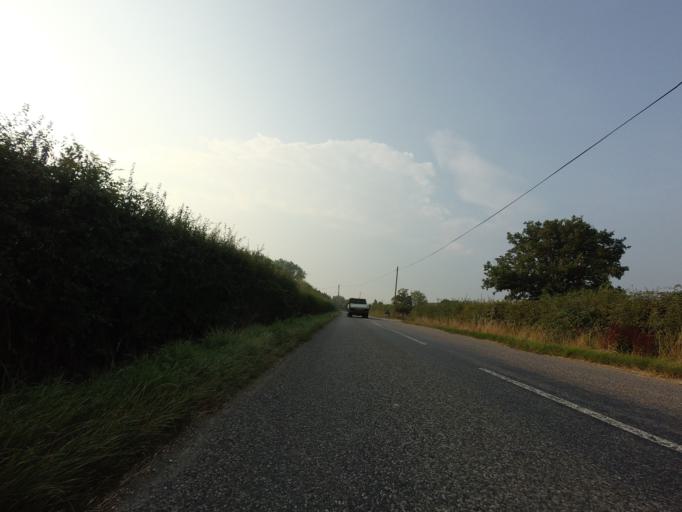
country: GB
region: England
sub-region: Kent
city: Ashford
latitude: 51.1276
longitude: 0.8217
